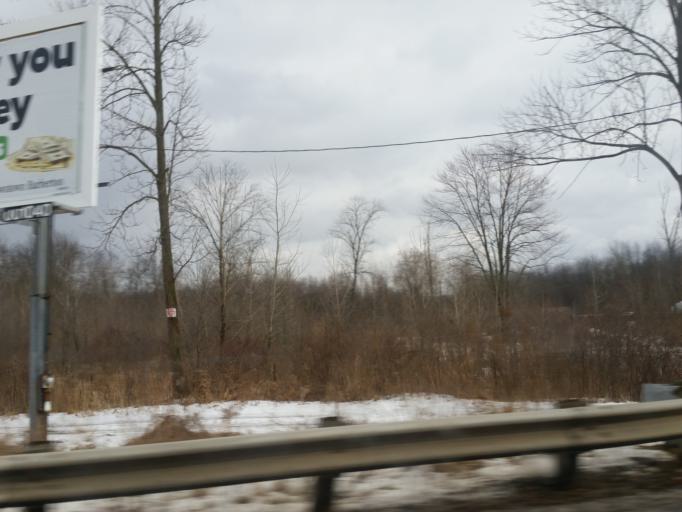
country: US
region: Ohio
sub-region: Summit County
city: Barberton
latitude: 41.0342
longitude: -81.6088
